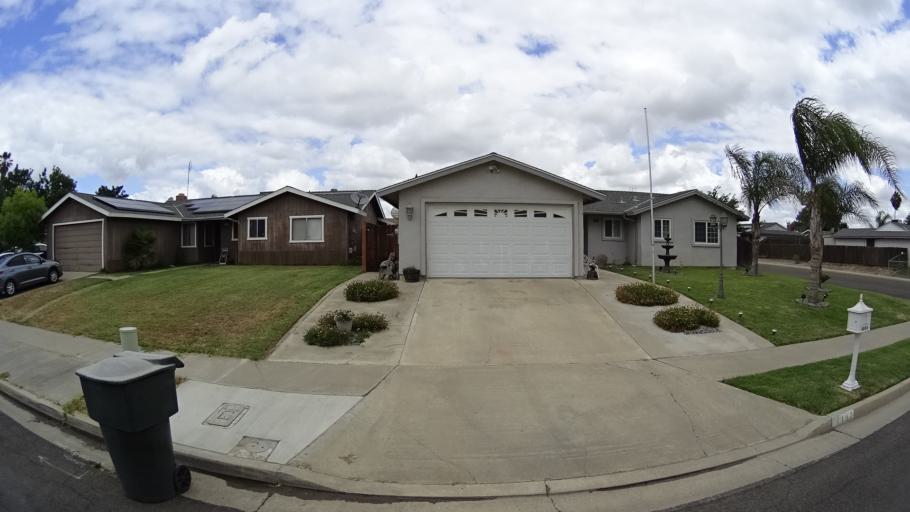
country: US
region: California
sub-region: Kings County
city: Hanford
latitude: 36.3345
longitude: -119.6267
